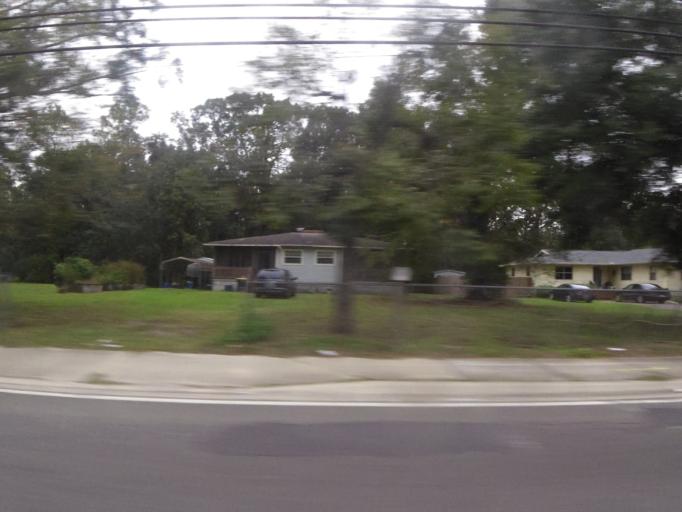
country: US
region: Florida
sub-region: Clay County
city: Bellair-Meadowbrook Terrace
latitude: 30.2702
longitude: -81.7534
